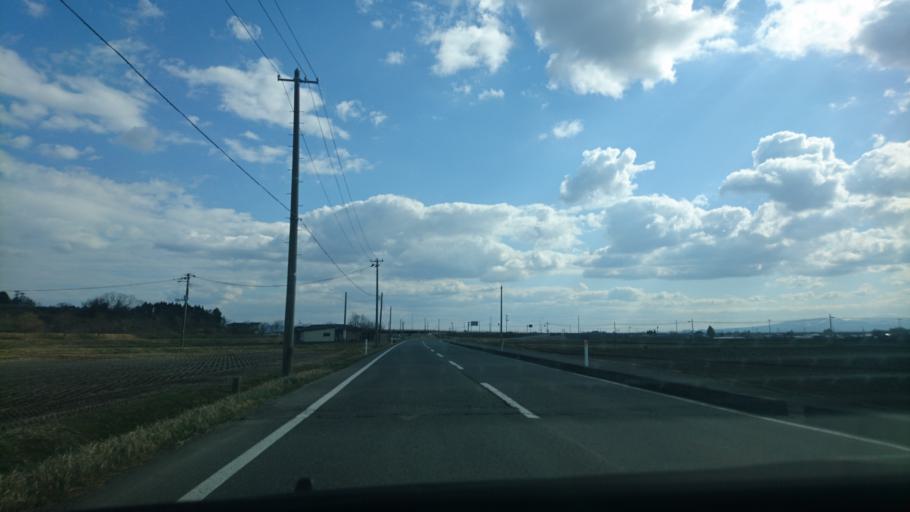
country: JP
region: Iwate
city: Mizusawa
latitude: 39.2095
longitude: 141.1599
